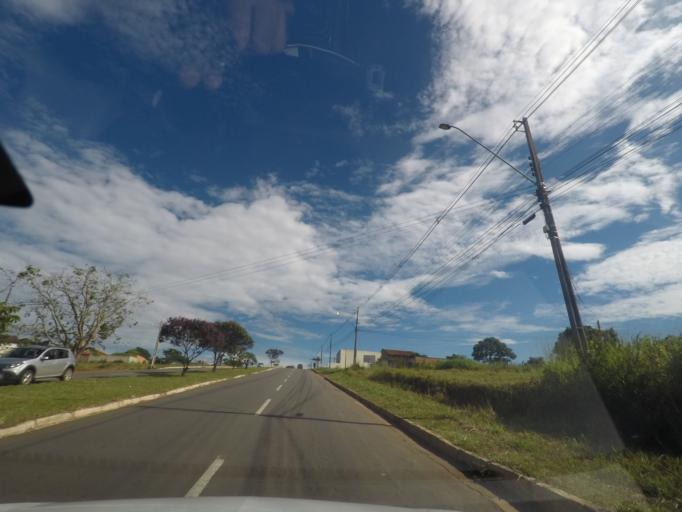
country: BR
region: Goias
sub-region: Aparecida De Goiania
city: Aparecida de Goiania
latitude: -16.8140
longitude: -49.2801
